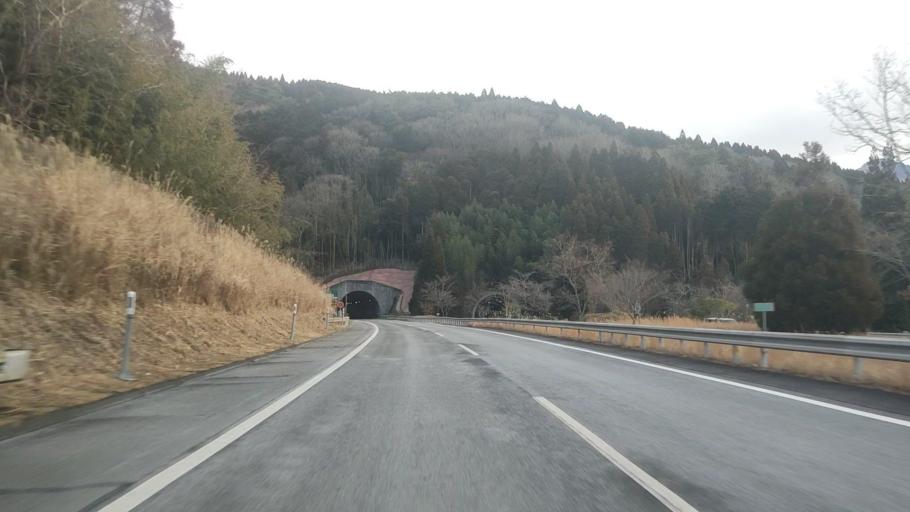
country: JP
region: Oita
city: Beppu
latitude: 33.2670
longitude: 131.3386
